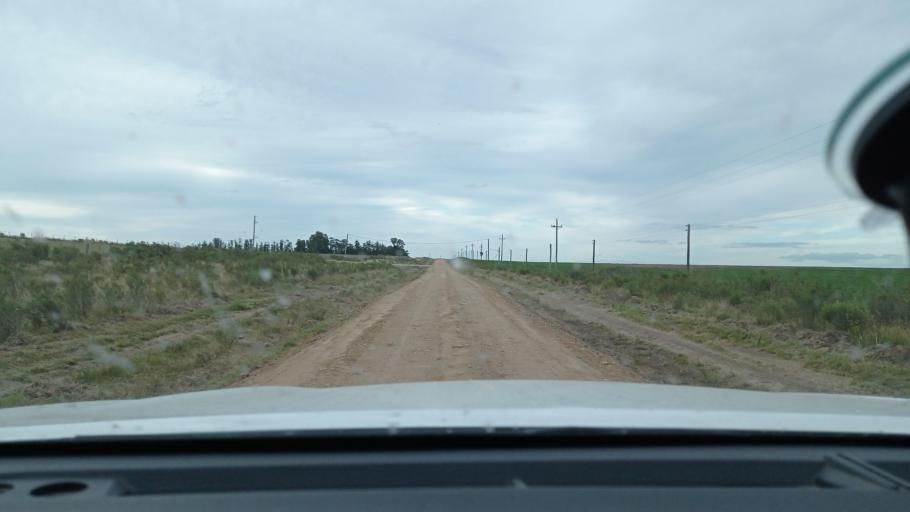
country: UY
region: Florida
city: Casupa
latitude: -34.1165
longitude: -55.7686
